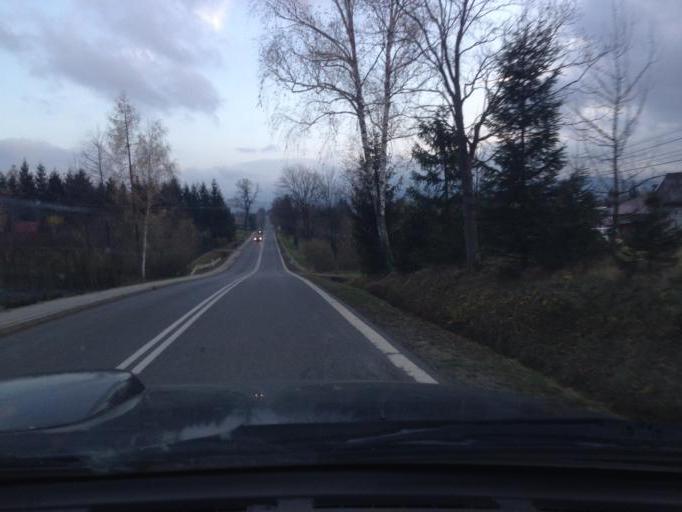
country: PL
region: Subcarpathian Voivodeship
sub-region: Powiat jasielski
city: Nowy Zmigrod
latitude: 49.6372
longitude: 21.5238
